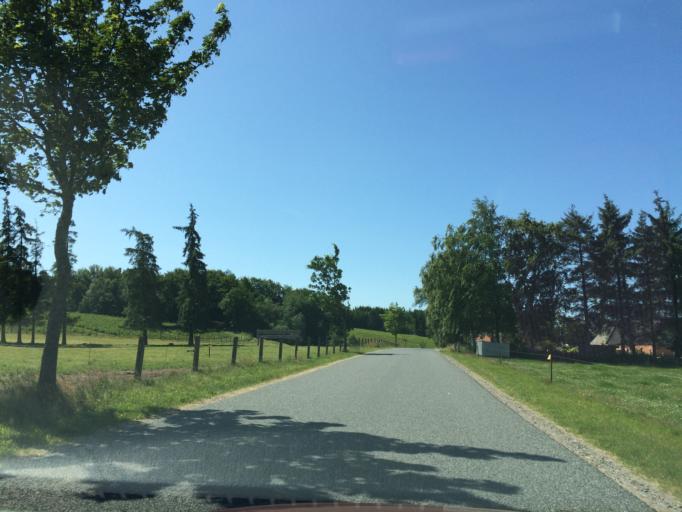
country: DK
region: Central Jutland
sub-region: Silkeborg Kommune
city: Svejbaek
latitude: 56.2105
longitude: 9.7169
